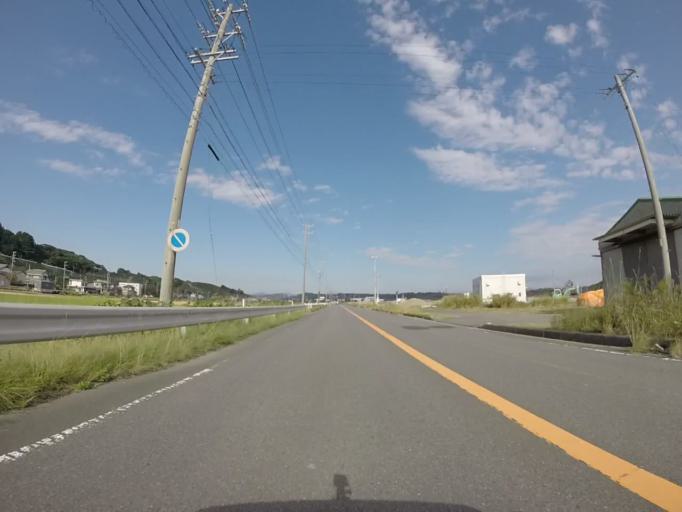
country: JP
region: Shizuoka
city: Shimada
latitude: 34.7659
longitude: 138.2364
